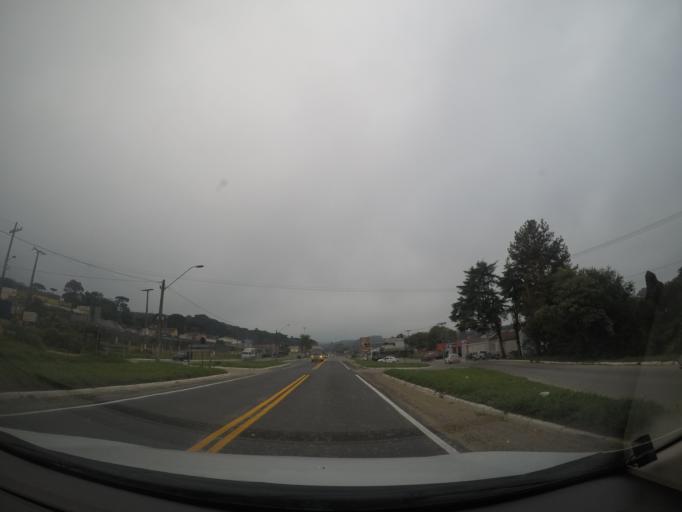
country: BR
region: Parana
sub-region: Almirante Tamandare
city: Almirante Tamandare
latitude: -25.3457
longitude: -49.2832
